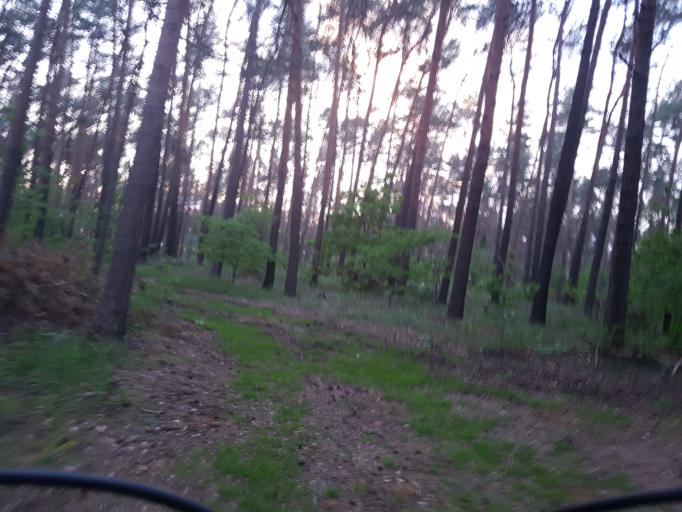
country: DE
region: Brandenburg
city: Trobitz
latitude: 51.5663
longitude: 13.4189
